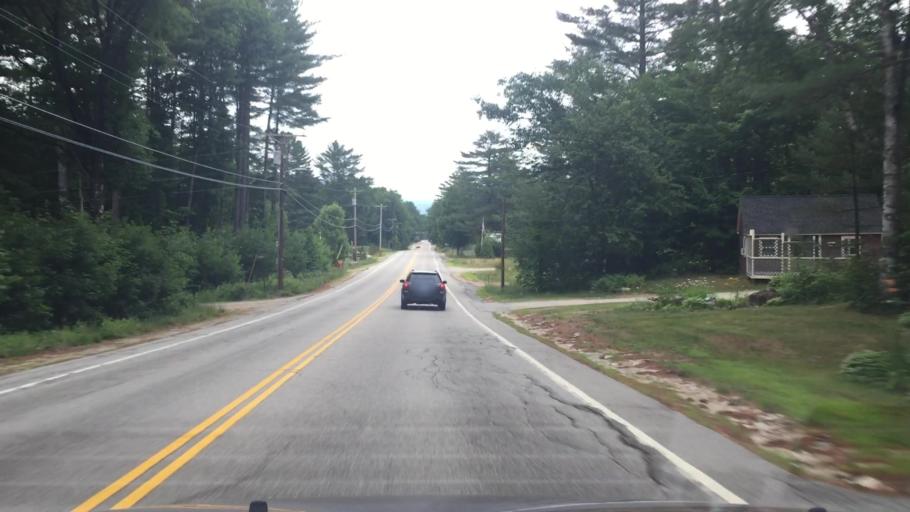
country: US
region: New Hampshire
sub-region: Carroll County
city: North Conway
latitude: 44.0757
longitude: -71.2941
